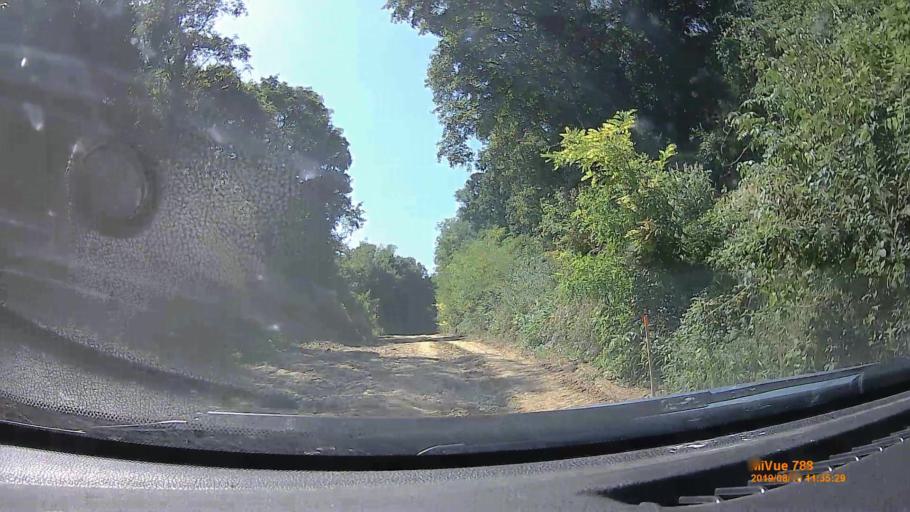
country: HU
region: Somogy
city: Somogyvar
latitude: 46.5161
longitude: 17.7770
